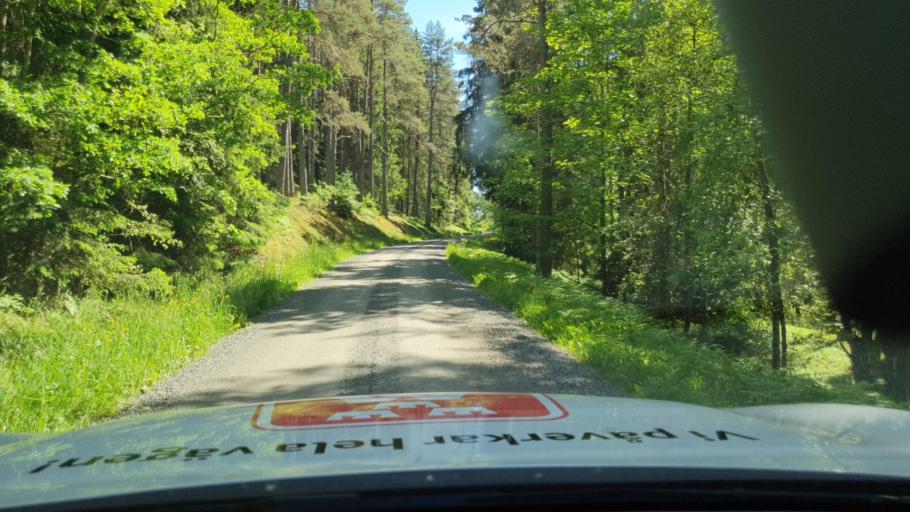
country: SE
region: Joenkoeping
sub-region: Mullsjo Kommun
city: Mullsjoe
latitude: 58.0455
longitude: 13.8749
